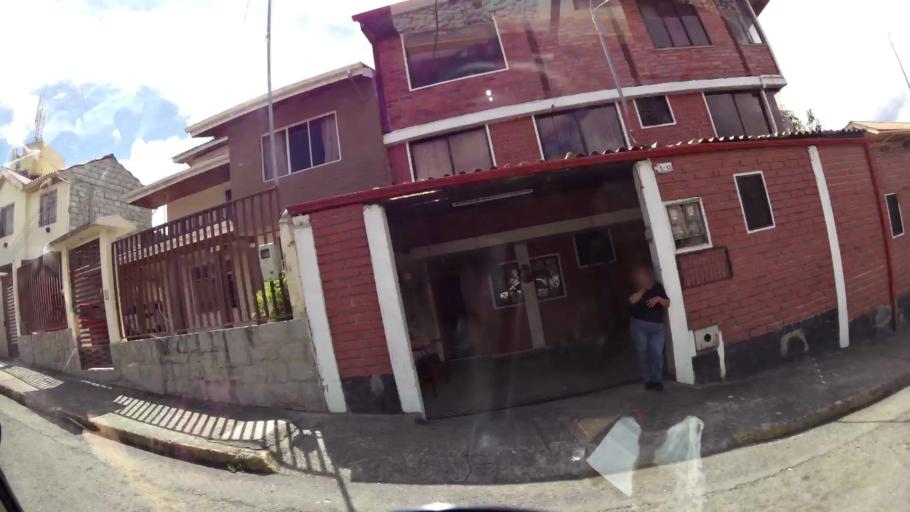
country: EC
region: Canar
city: Azogues
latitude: -2.7378
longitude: -78.8426
